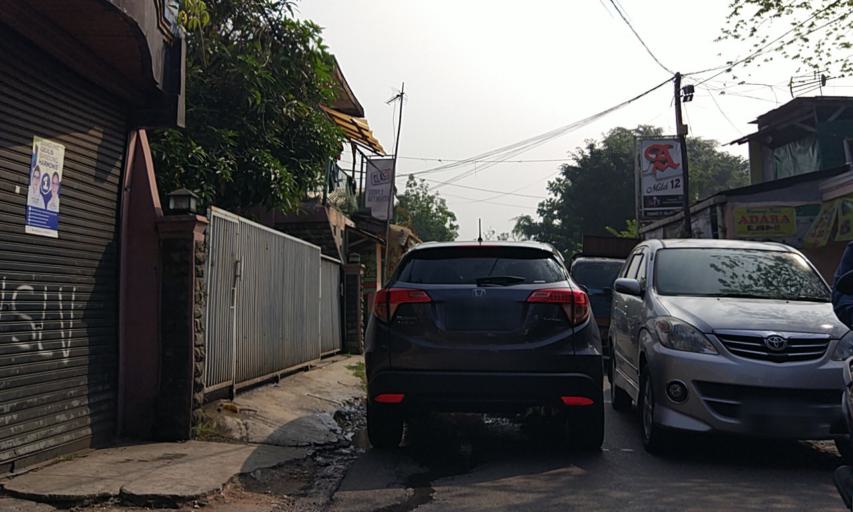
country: ID
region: West Java
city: Bandung
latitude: -6.9048
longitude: 107.6490
